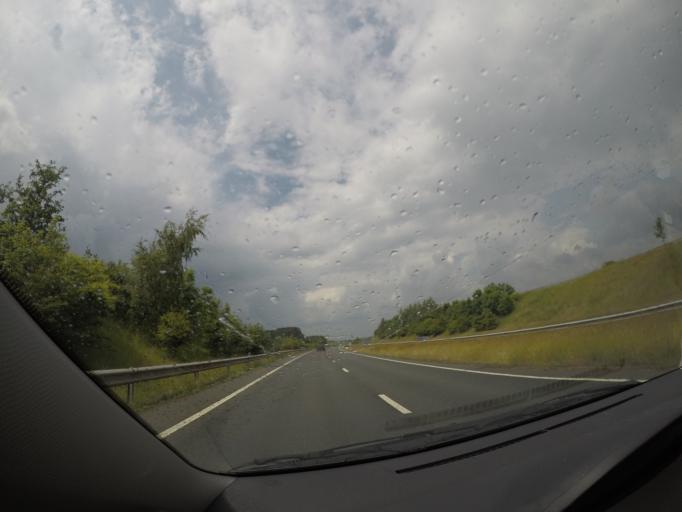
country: GB
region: England
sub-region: Cumbria
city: Appleby-in-Westmorland
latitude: 54.6372
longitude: -2.6122
